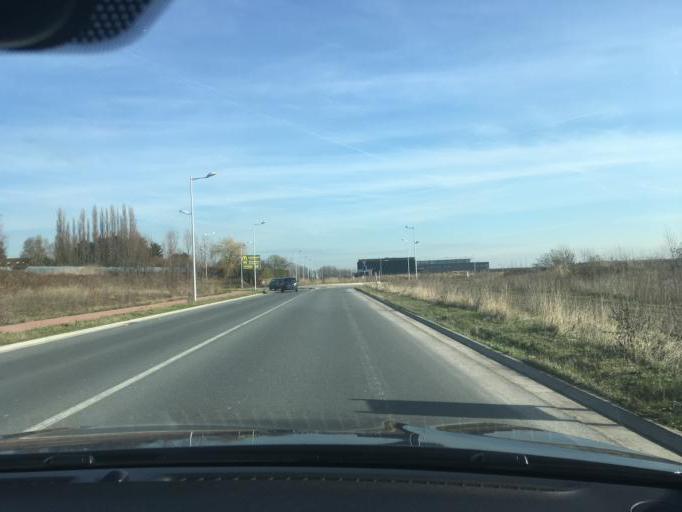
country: BE
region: Wallonia
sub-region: Province du Hainaut
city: Estaimpuis
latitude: 50.7204
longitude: 3.2887
